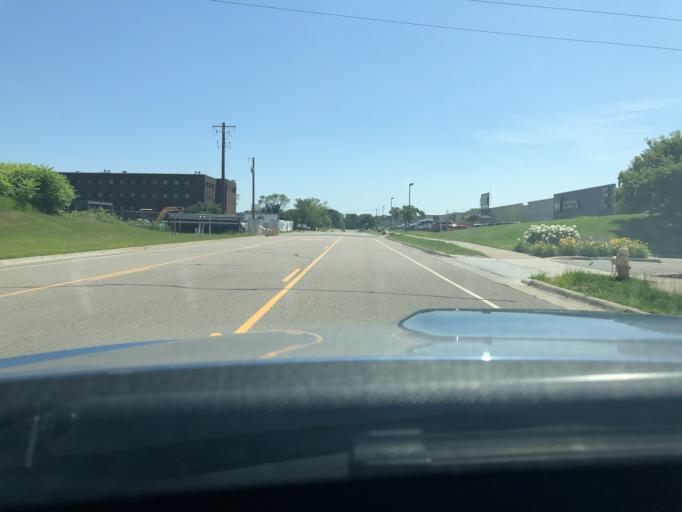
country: US
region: Minnesota
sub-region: Ramsey County
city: Roseville
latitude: 45.0173
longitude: -93.1823
